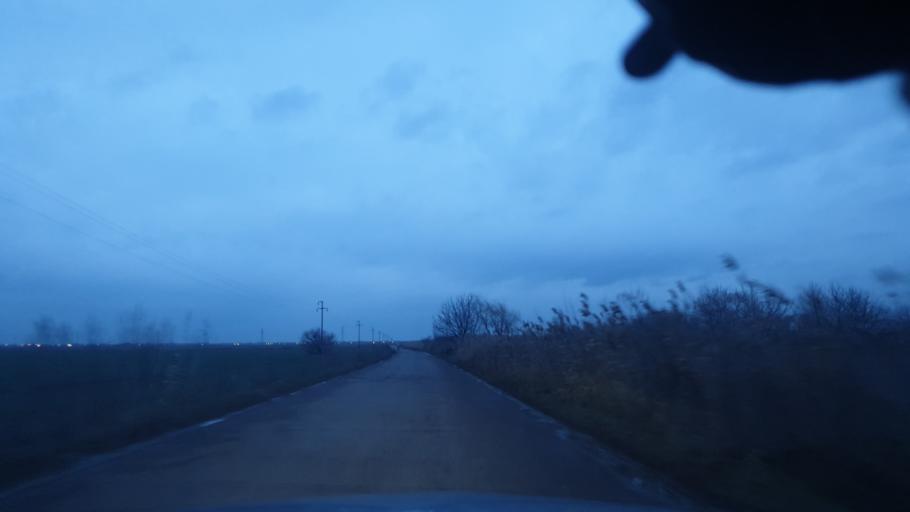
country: RS
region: Autonomna Pokrajina Vojvodina
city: Nova Pazova
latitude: 44.9250
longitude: 20.2162
